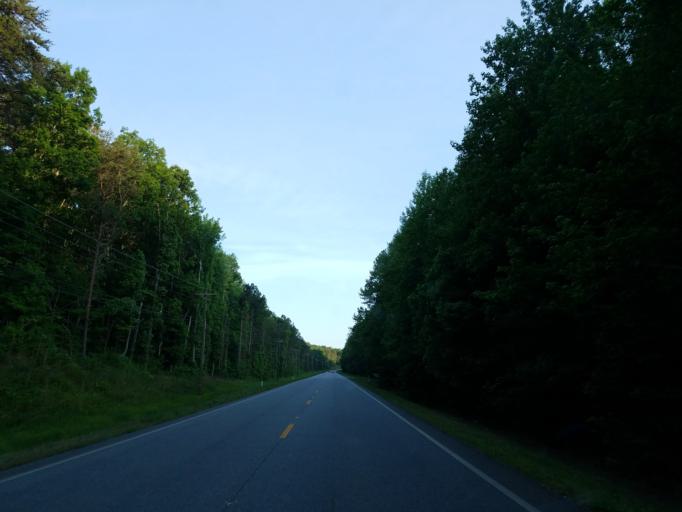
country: US
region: Georgia
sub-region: Whitfield County
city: Dalton
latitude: 34.6715
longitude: -85.0620
